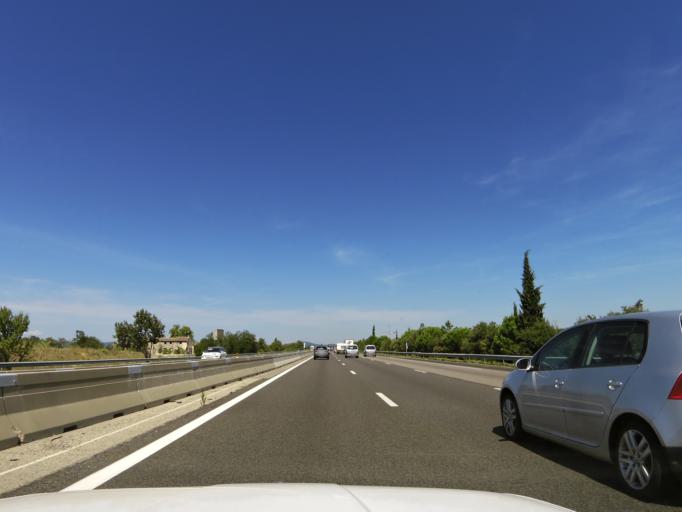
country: FR
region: Rhone-Alpes
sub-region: Departement de la Drome
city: Saint-Paul-Trois-Chateaux
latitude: 44.3403
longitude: 4.7380
